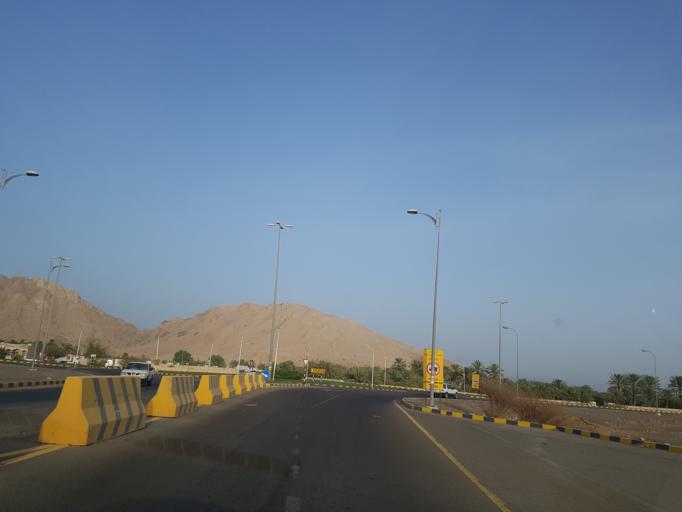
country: OM
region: Al Buraimi
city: Al Buraymi
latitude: 24.2305
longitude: 55.9566
